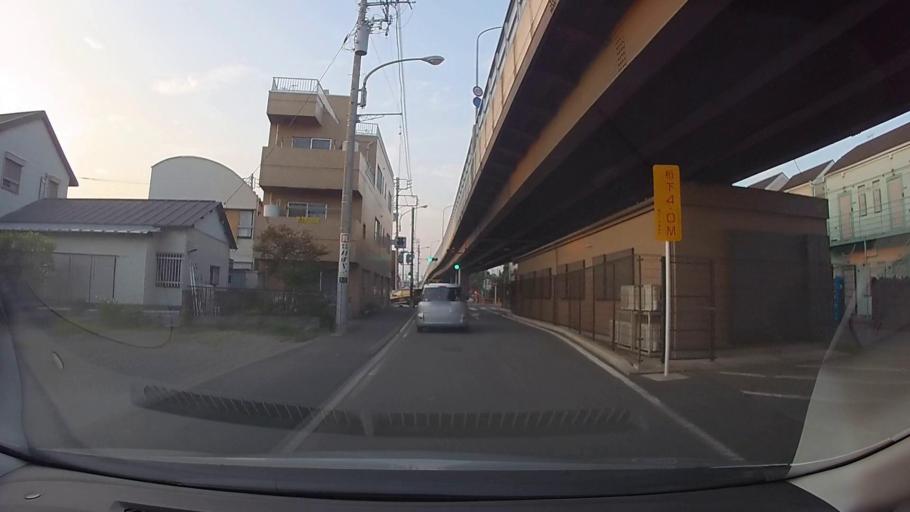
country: JP
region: Kanagawa
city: Minami-rinkan
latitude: 35.4690
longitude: 139.4804
